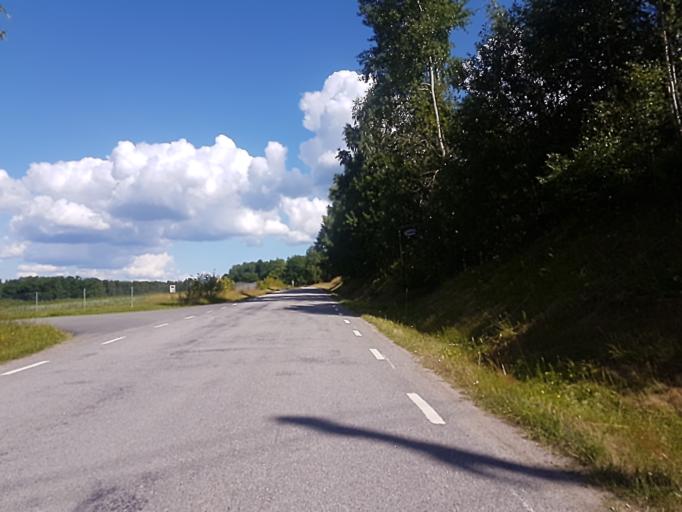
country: SE
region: Soedermanland
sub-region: Gnesta Kommun
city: Gnesta
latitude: 59.0463
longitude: 17.3382
